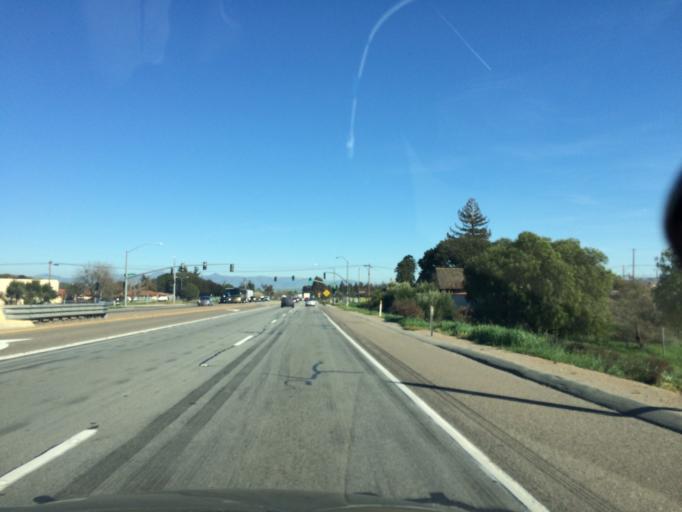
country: US
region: California
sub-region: San Benito County
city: San Juan Bautista
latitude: 36.8406
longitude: -121.5351
